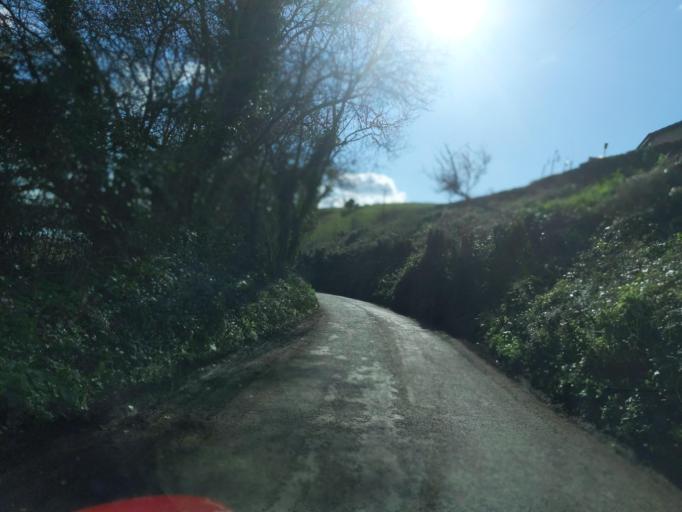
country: GB
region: England
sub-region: Devon
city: Kingsbridge
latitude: 50.2847
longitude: -3.7587
